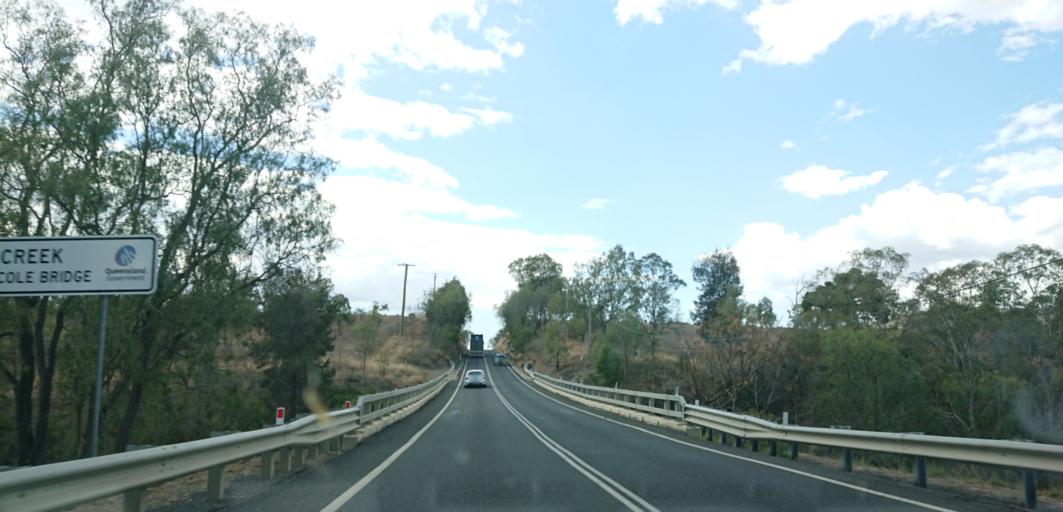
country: AU
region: Queensland
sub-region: Lockyer Valley
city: Gatton
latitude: -27.6604
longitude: 152.1636
